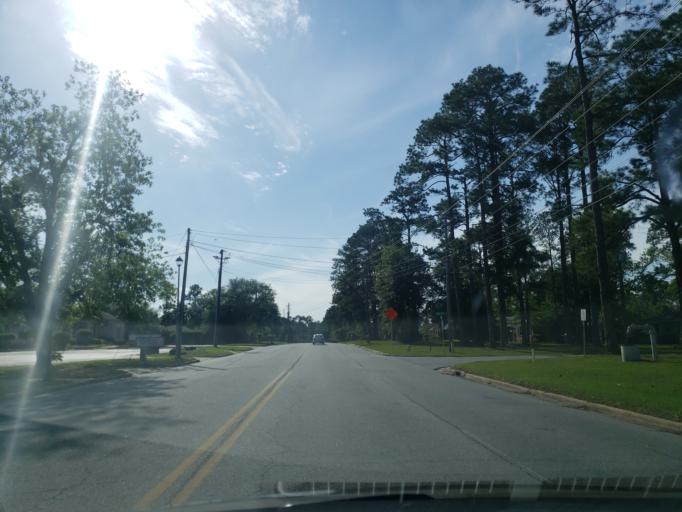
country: US
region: Georgia
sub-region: Dougherty County
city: Albany
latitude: 31.5909
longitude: -84.1867
